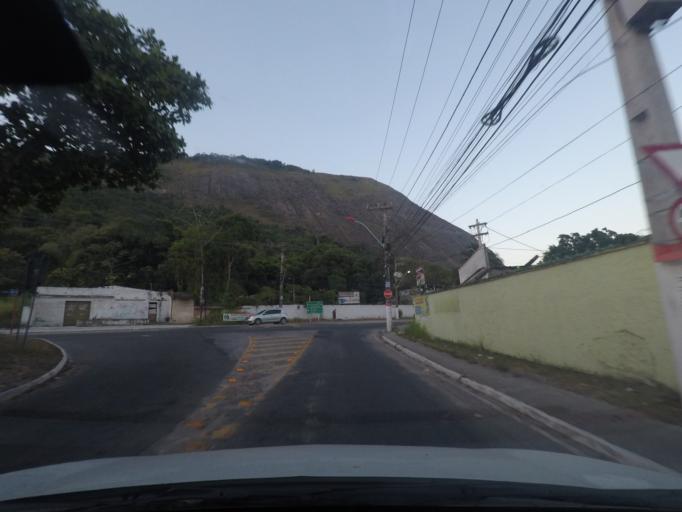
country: BR
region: Rio de Janeiro
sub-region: Marica
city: Marica
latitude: -22.9451
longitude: -42.9623
